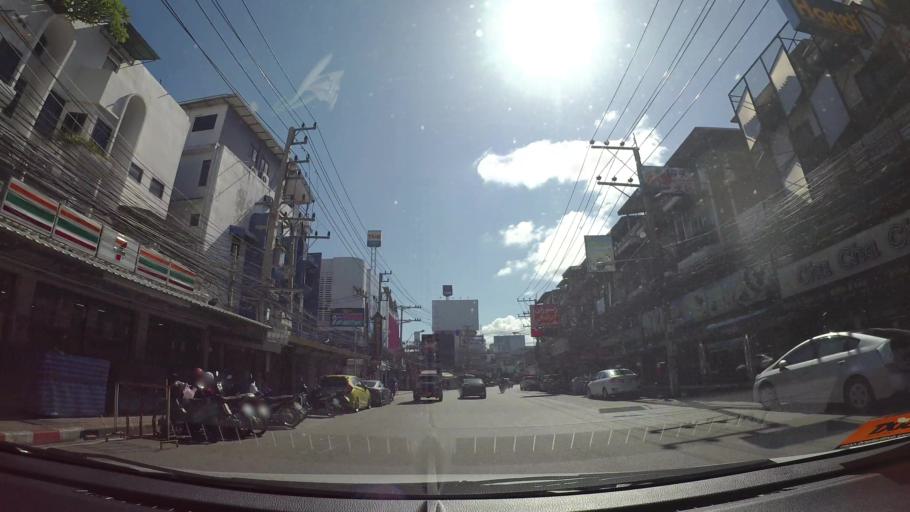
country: TH
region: Chon Buri
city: Phatthaya
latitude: 12.9272
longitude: 100.8765
